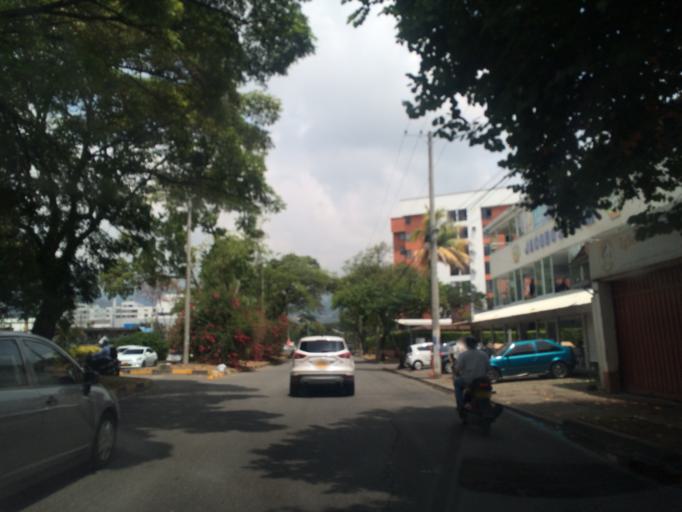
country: CO
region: Valle del Cauca
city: Cali
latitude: 3.3934
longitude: -76.5367
